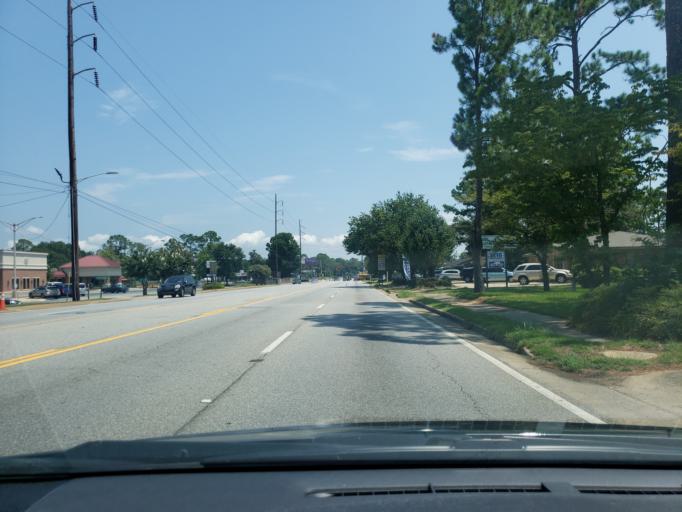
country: US
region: Georgia
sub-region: Dougherty County
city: Albany
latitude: 31.5812
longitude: -84.1930
